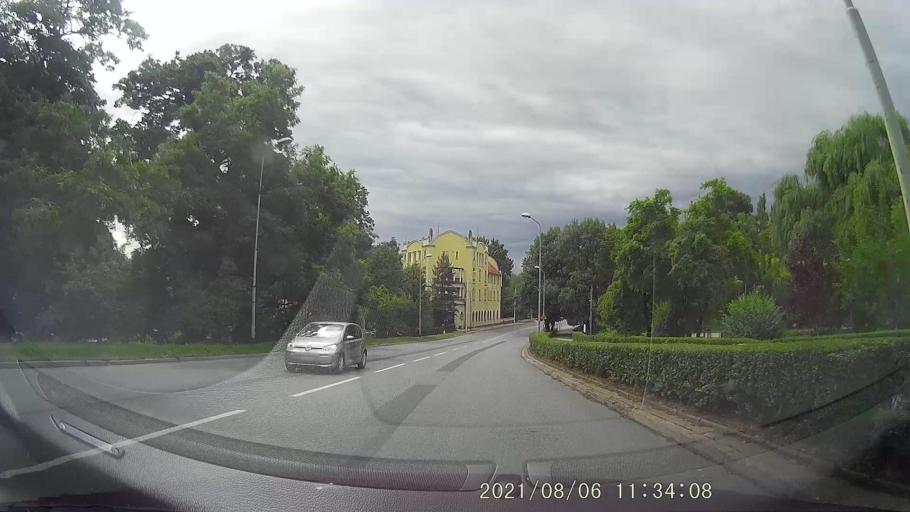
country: PL
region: Lower Silesian Voivodeship
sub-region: Powiat klodzki
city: Klodzko
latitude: 50.4386
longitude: 16.6488
